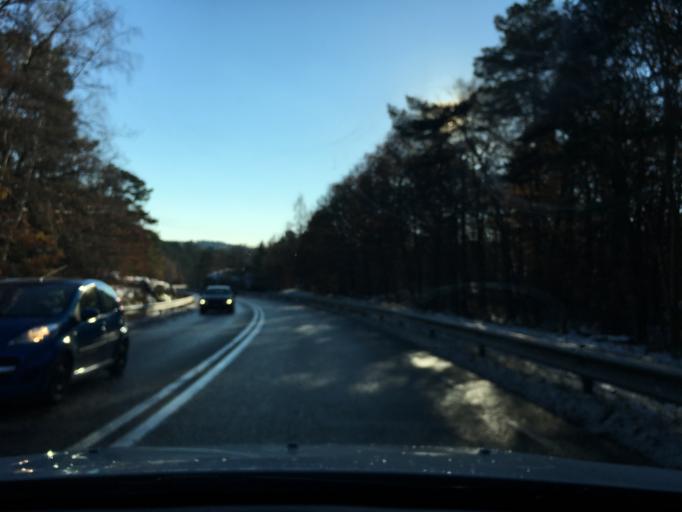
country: SE
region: Vaestra Goetaland
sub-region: Tjorns Kommun
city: Myggenas
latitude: 58.0814
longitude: 11.6945
